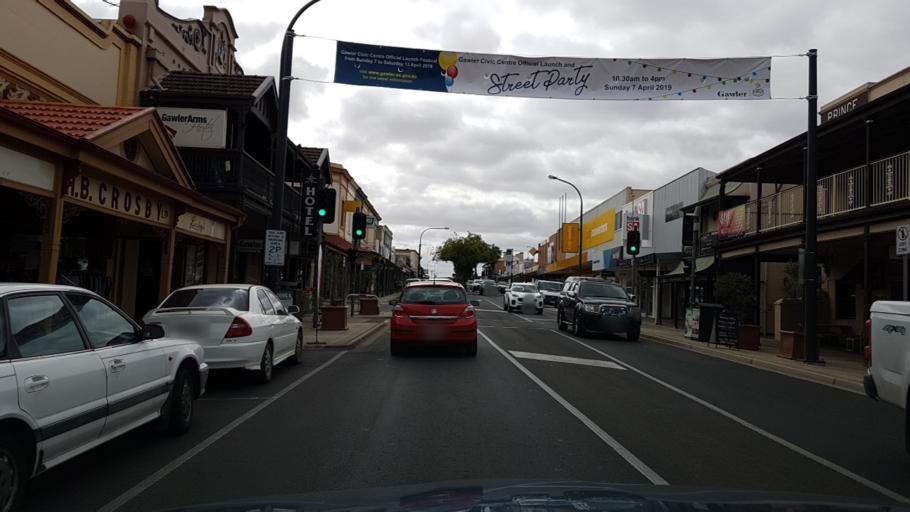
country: AU
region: South Australia
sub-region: Gawler
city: Gawler
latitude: -34.5987
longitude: 138.7484
